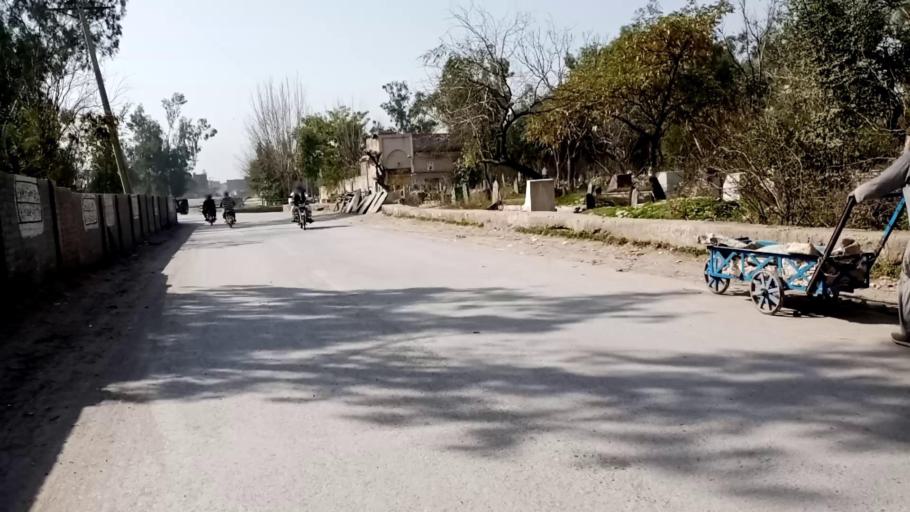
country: PK
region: Khyber Pakhtunkhwa
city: Peshawar
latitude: 33.9963
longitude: 71.5857
